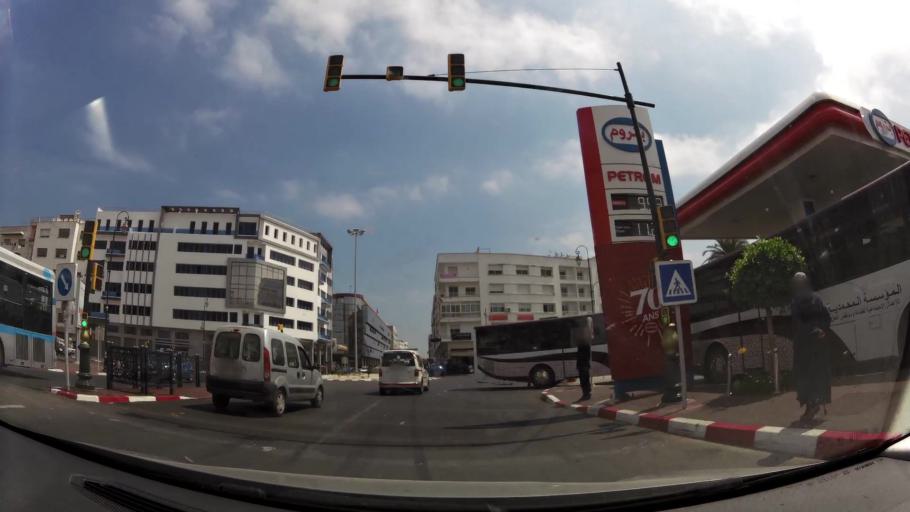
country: MA
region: Rabat-Sale-Zemmour-Zaer
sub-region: Rabat
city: Rabat
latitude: 34.0182
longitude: -6.8442
